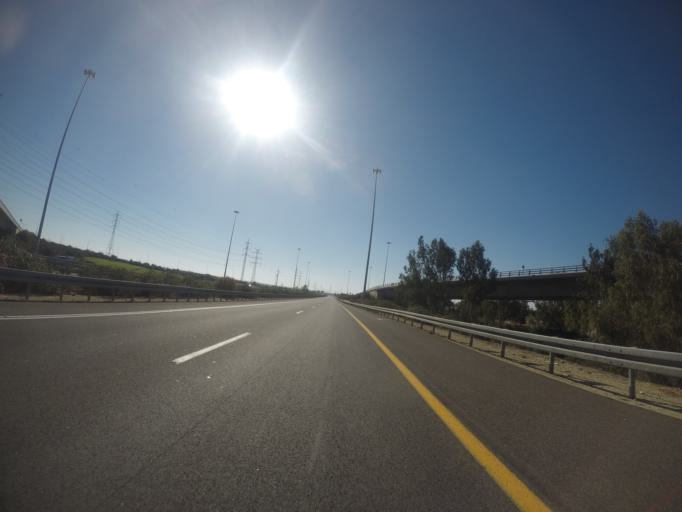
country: IL
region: Southern District
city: Ashdod
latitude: 31.7759
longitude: 34.6673
